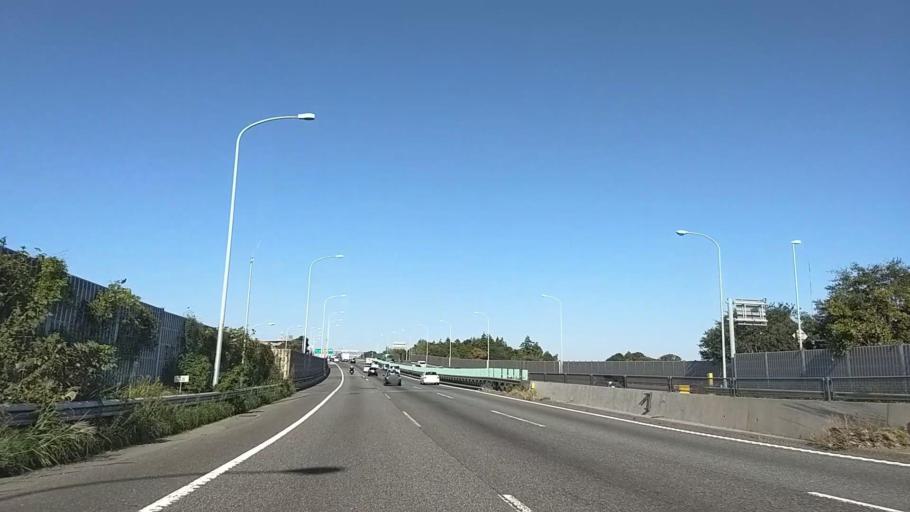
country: JP
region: Kanagawa
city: Minami-rinkan
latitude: 35.4617
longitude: 139.5431
